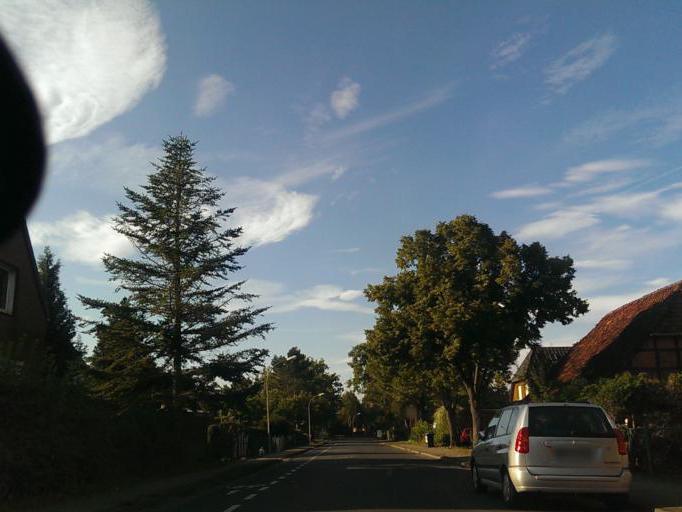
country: DE
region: Lower Saxony
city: Garbsen-Mitte
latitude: 52.4657
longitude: 9.6101
